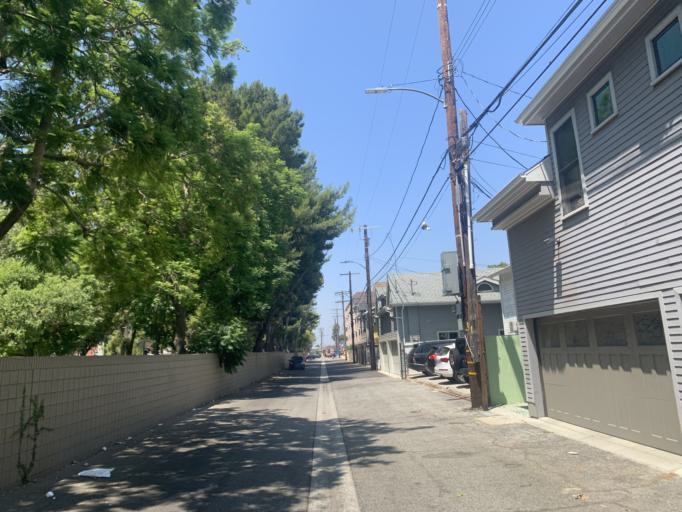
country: US
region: California
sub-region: Los Angeles County
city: Los Angeles
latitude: 34.0269
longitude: -118.2891
